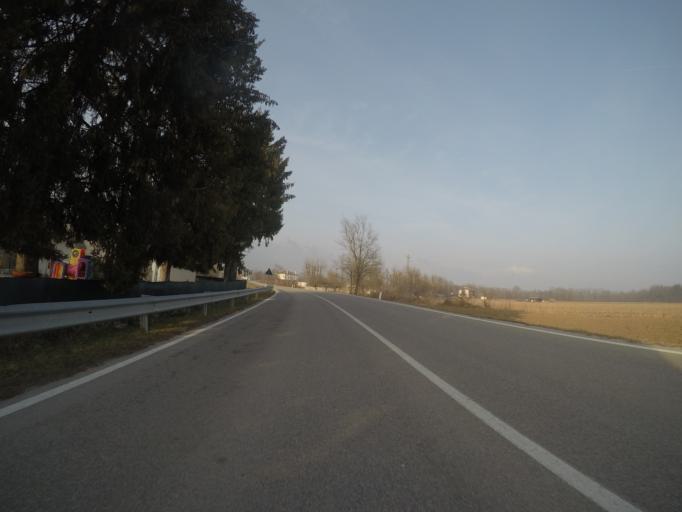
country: IT
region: Veneto
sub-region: Provincia di Belluno
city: Sedico
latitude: 46.1005
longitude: 12.0672
